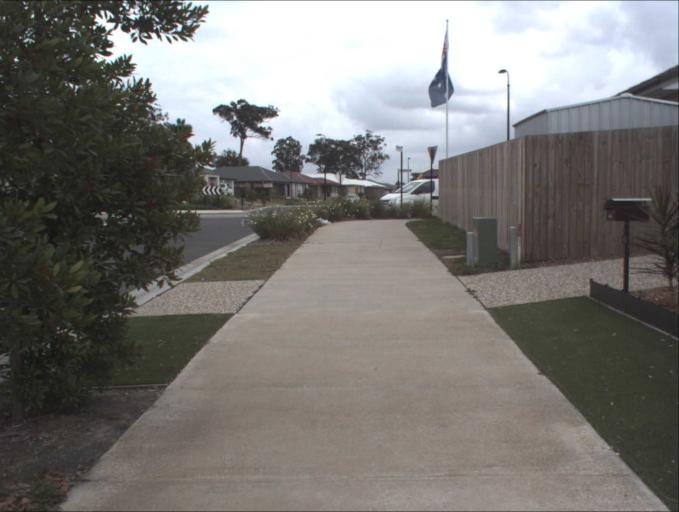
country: AU
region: Queensland
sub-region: Logan
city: Logan Reserve
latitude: -27.7112
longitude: 153.1122
